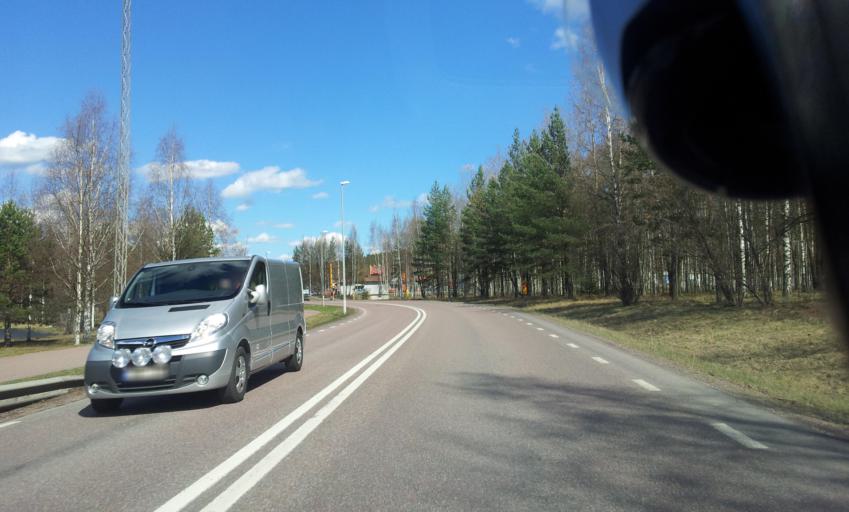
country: SE
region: Dalarna
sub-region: Faluns Kommun
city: Falun
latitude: 60.6207
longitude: 15.6149
